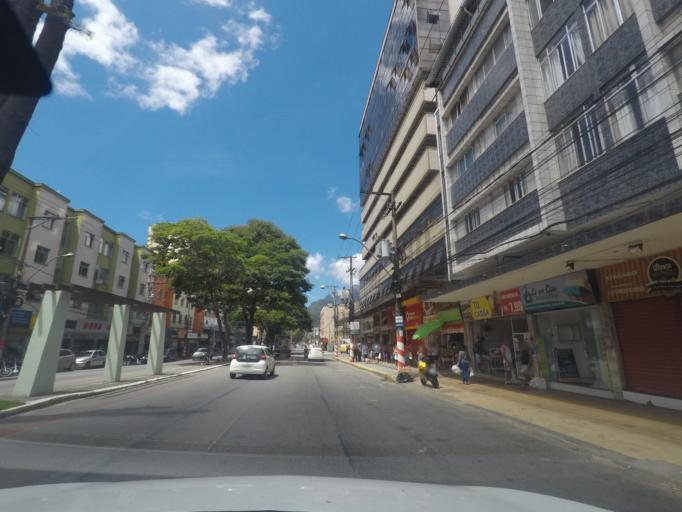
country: BR
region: Rio de Janeiro
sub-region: Teresopolis
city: Teresopolis
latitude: -22.4146
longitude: -42.9709
